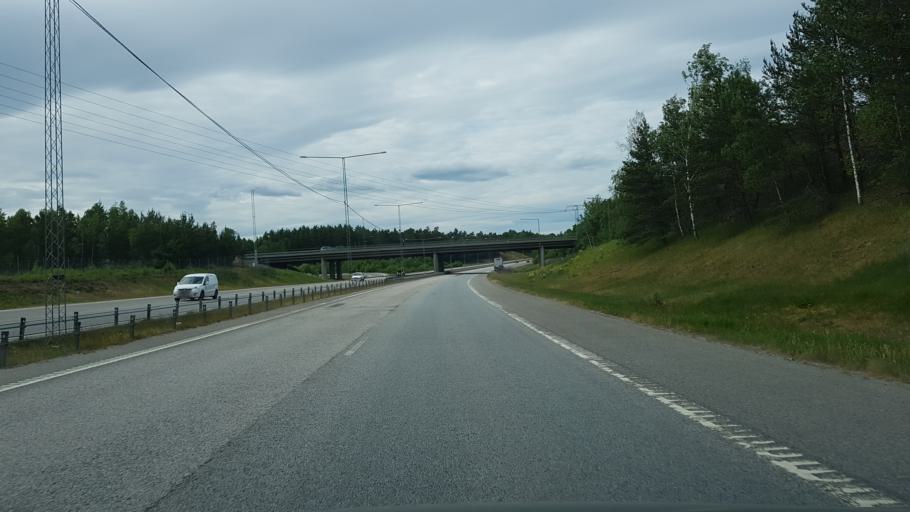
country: SE
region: Stockholm
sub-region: Haninge Kommun
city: Haninge
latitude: 59.1525
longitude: 18.1554
